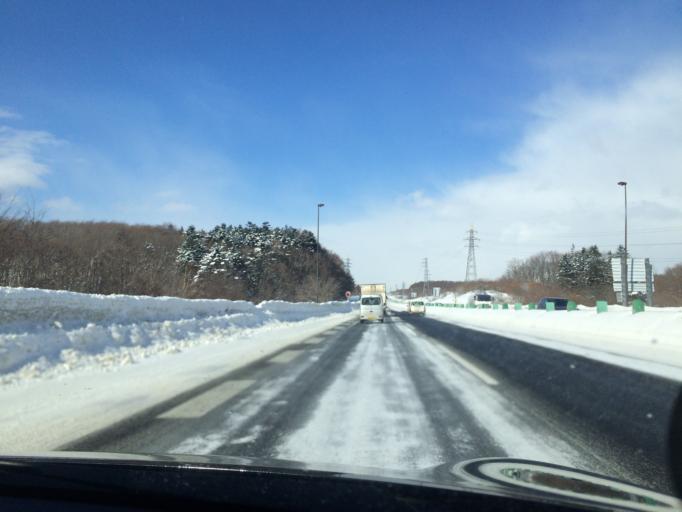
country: JP
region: Hokkaido
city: Kitahiroshima
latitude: 42.9537
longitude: 141.5091
